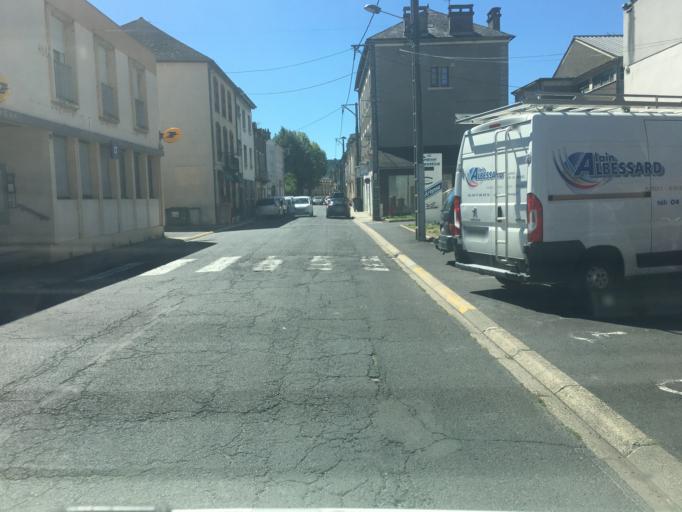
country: FR
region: Limousin
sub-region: Departement de la Correze
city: Bort-les-Orgues
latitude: 45.4029
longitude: 2.4992
